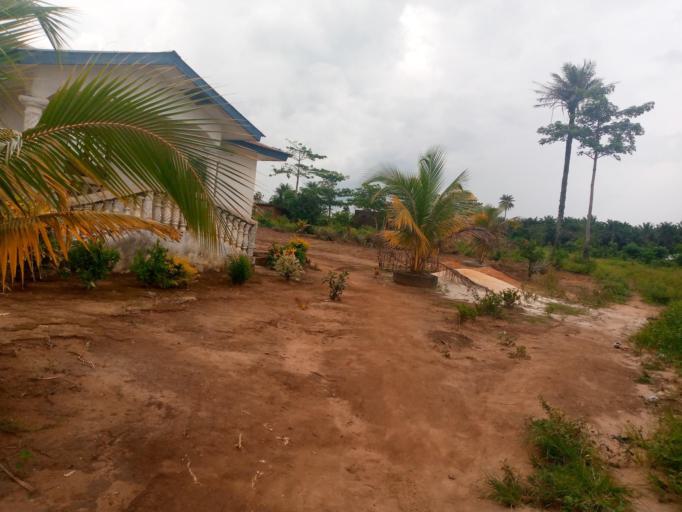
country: SL
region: Southern Province
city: Sumbuya
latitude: 7.5993
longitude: -12.1602
